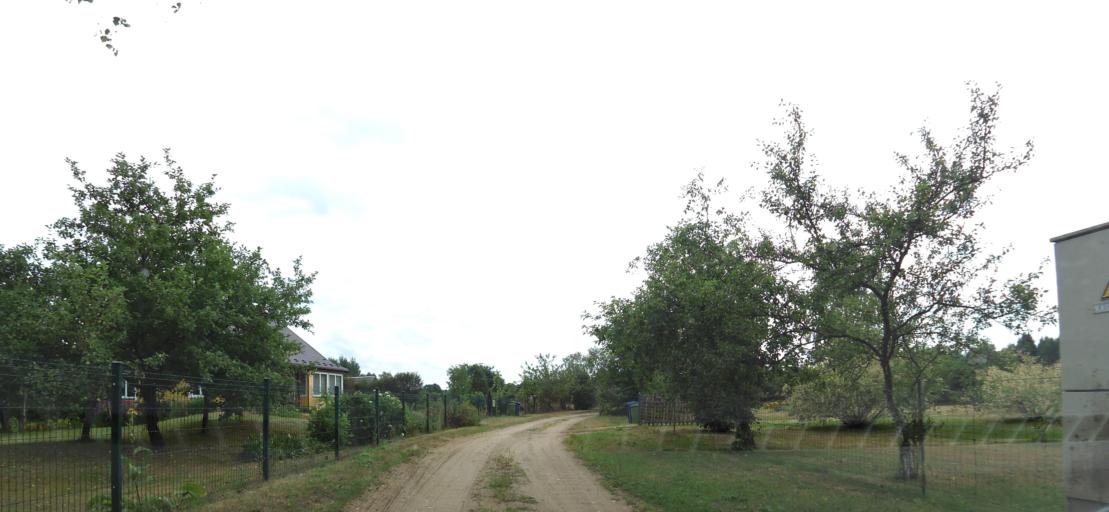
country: LT
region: Alytaus apskritis
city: Varena
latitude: 54.0204
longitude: 24.3330
